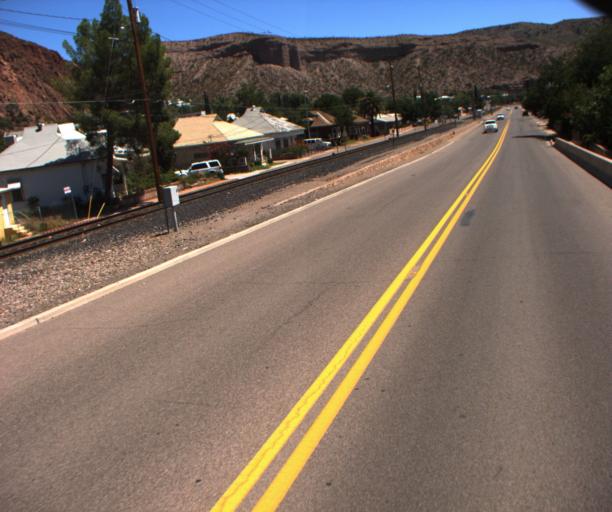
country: US
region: Arizona
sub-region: Greenlee County
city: Clifton
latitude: 33.0487
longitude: -109.2947
